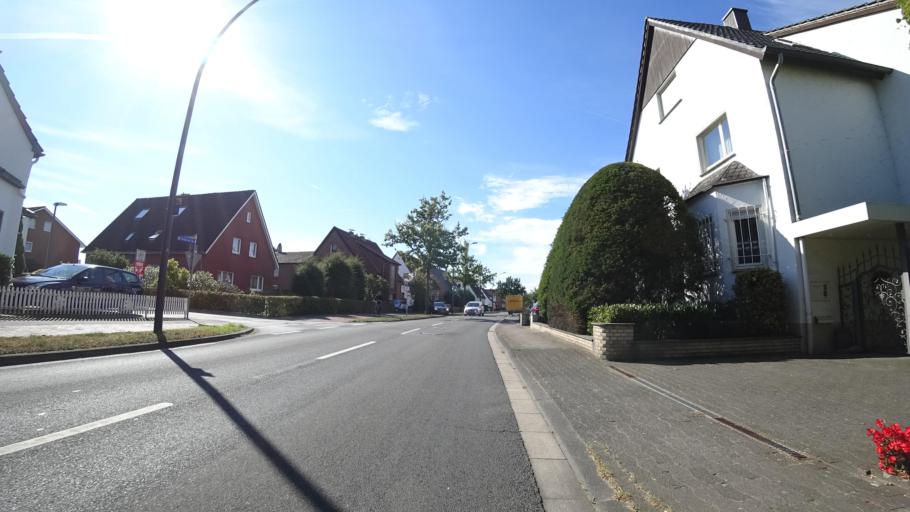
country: DE
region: North Rhine-Westphalia
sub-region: Regierungsbezirk Detmold
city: Guetersloh
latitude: 51.9237
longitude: 8.4305
